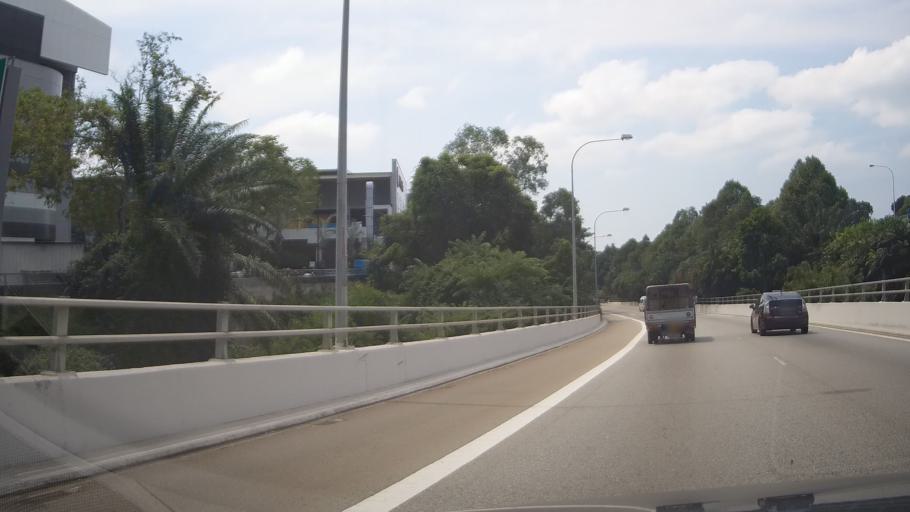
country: SG
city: Singapore
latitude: 1.3504
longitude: 103.9650
